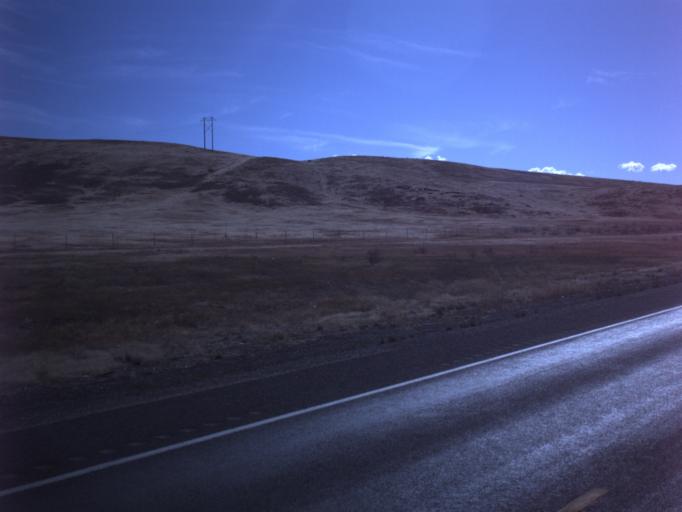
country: US
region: Utah
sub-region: Sanpete County
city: Gunnison
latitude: 39.1794
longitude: -111.8388
